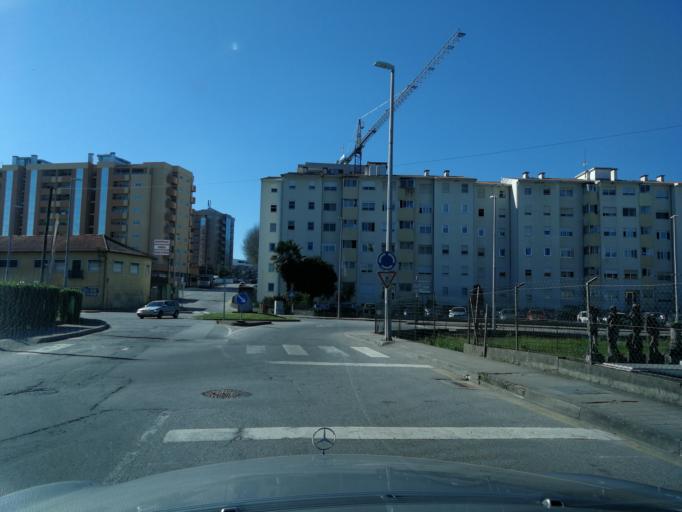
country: PT
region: Braga
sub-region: Vila Nova de Famalicao
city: Vila Nova de Famalicao
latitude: 41.4008
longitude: -8.5194
